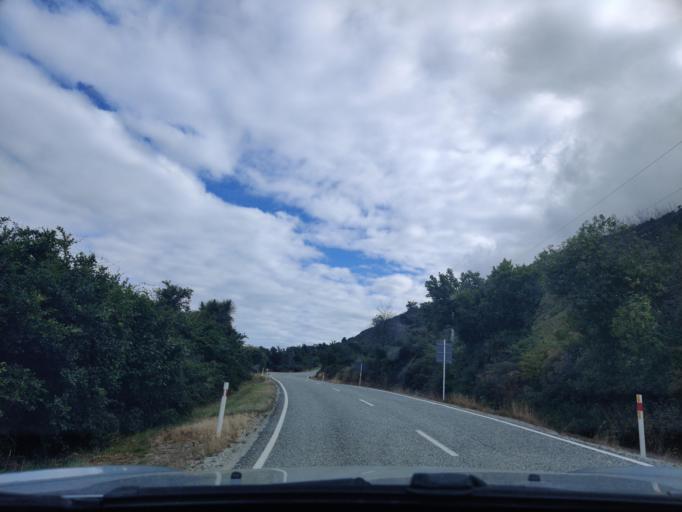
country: NZ
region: Otago
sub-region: Queenstown-Lakes District
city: Queenstown
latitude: -45.0763
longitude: 168.4660
